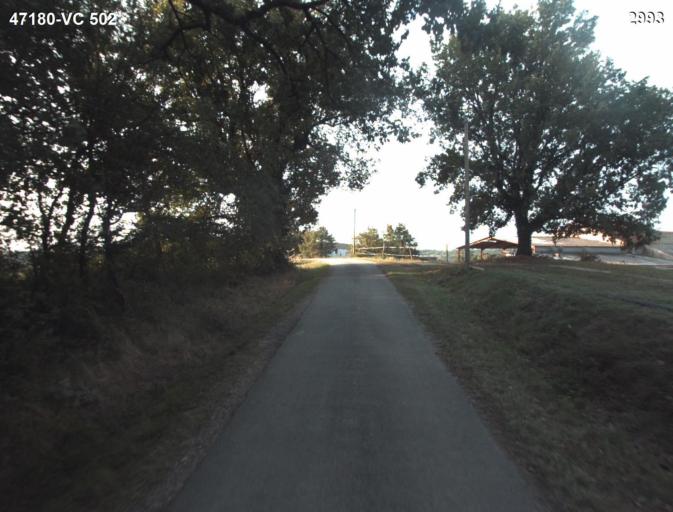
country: FR
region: Aquitaine
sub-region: Departement du Lot-et-Garonne
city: Sainte-Colombe-en-Bruilhois
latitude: 44.1836
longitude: 0.4826
